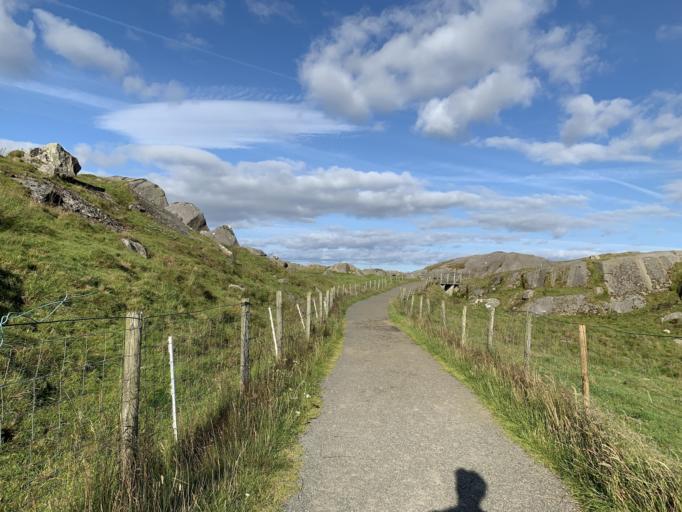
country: NO
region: Rogaland
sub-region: Eigersund
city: Egersund
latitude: 58.4416
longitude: 5.8830
